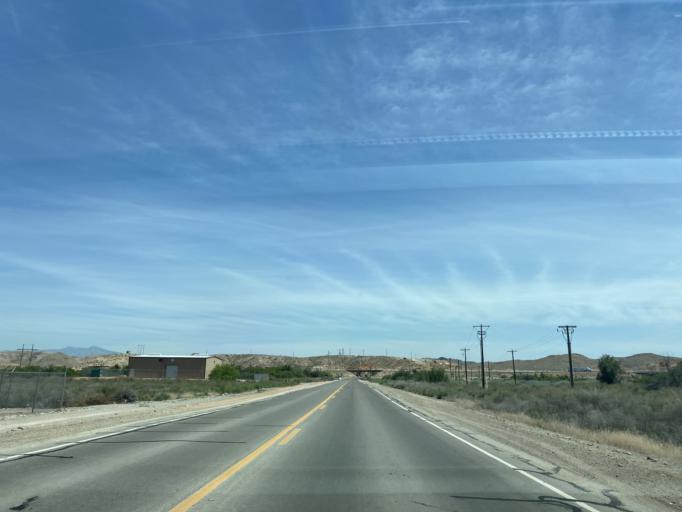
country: US
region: Nevada
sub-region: Clark County
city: Moapa Town
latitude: 36.6637
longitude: -114.5793
